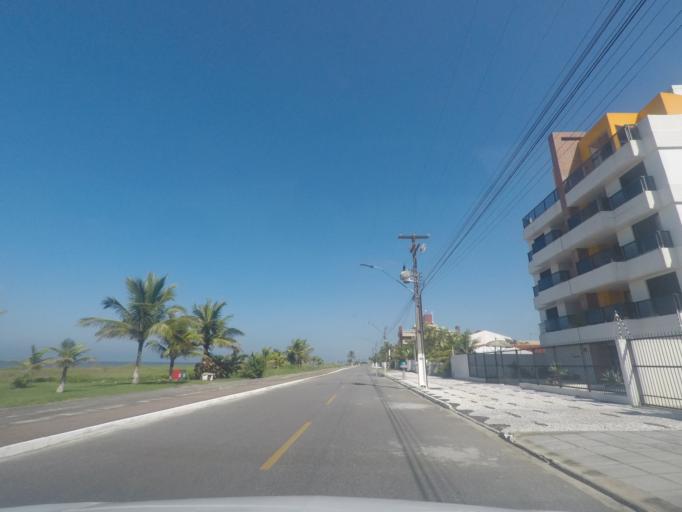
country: BR
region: Parana
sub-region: Pontal Do Parana
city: Pontal do Parana
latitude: -25.7256
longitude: -48.4856
